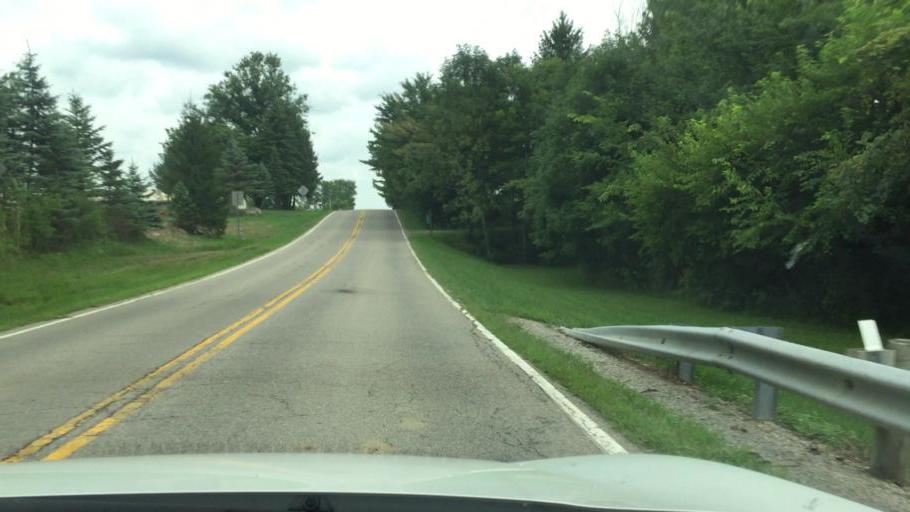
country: US
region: Ohio
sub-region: Champaign County
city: North Lewisburg
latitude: 40.2399
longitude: -83.4749
